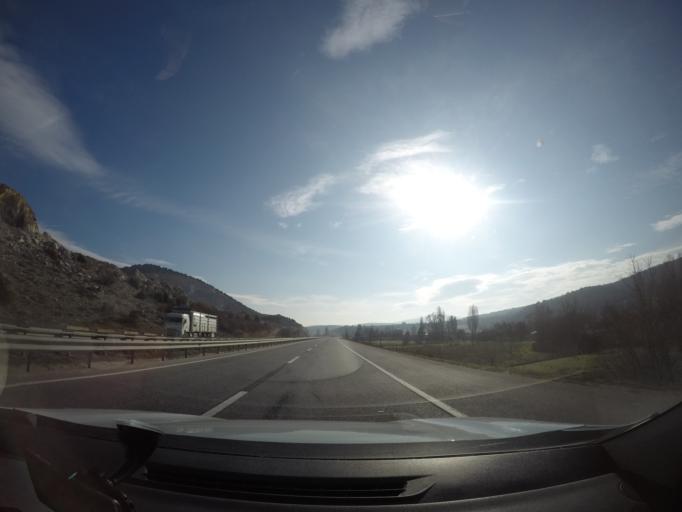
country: TR
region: Bilecik
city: Bozuyuk
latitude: 39.8946
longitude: 29.9632
